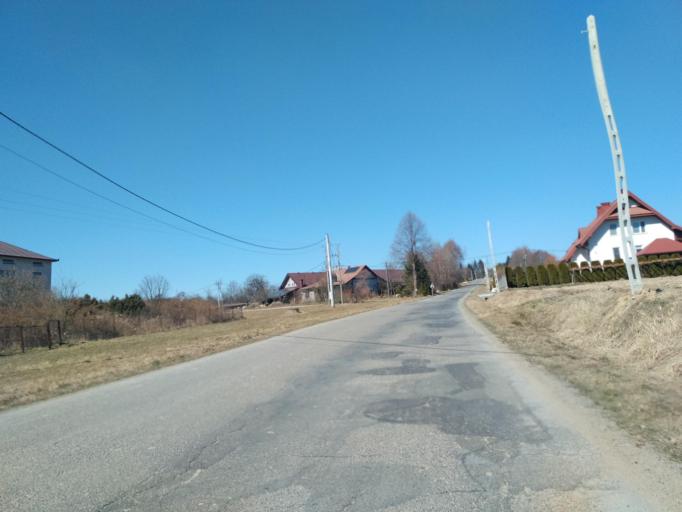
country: PL
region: Subcarpathian Voivodeship
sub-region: Powiat debicki
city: Brzostek
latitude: 49.9441
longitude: 21.4333
